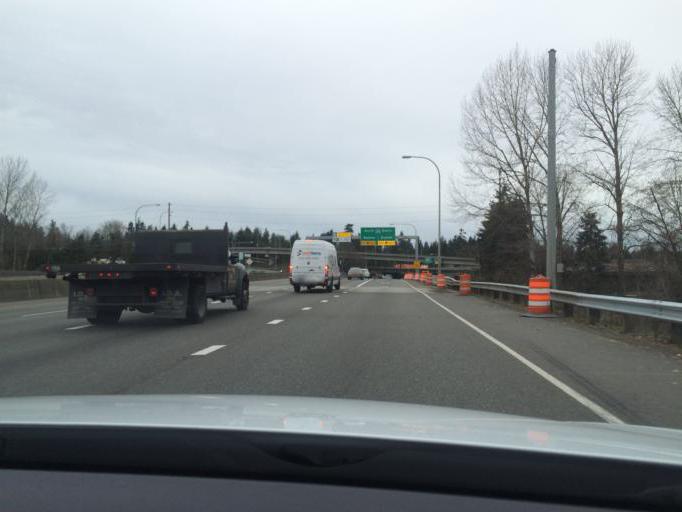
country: US
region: Washington
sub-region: King County
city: Bellevue
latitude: 47.6322
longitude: -122.1836
